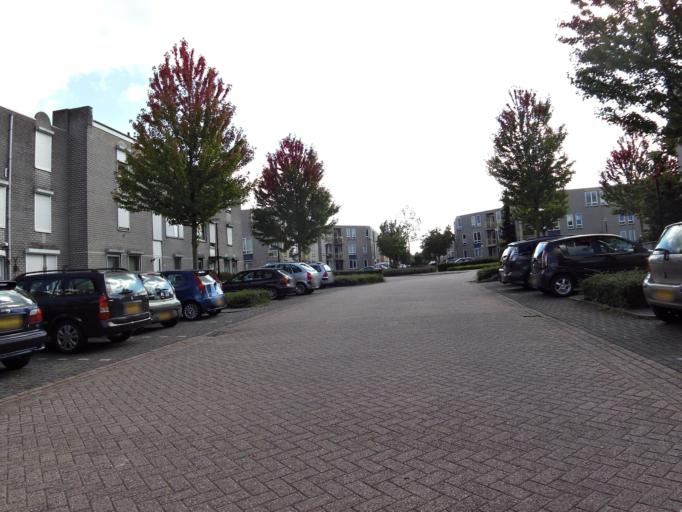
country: NL
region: Limburg
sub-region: Gemeente Heerlen
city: Heerlen
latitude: 50.9041
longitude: 6.0253
